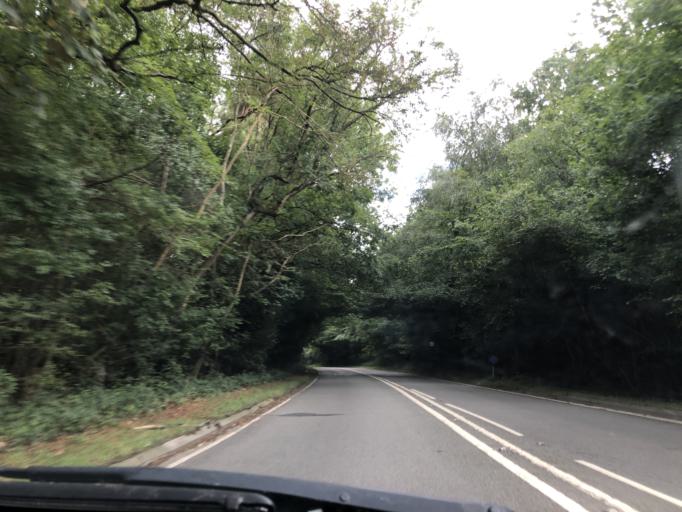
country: GB
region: England
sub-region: East Sussex
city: Forest Row
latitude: 51.0677
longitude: 0.0251
